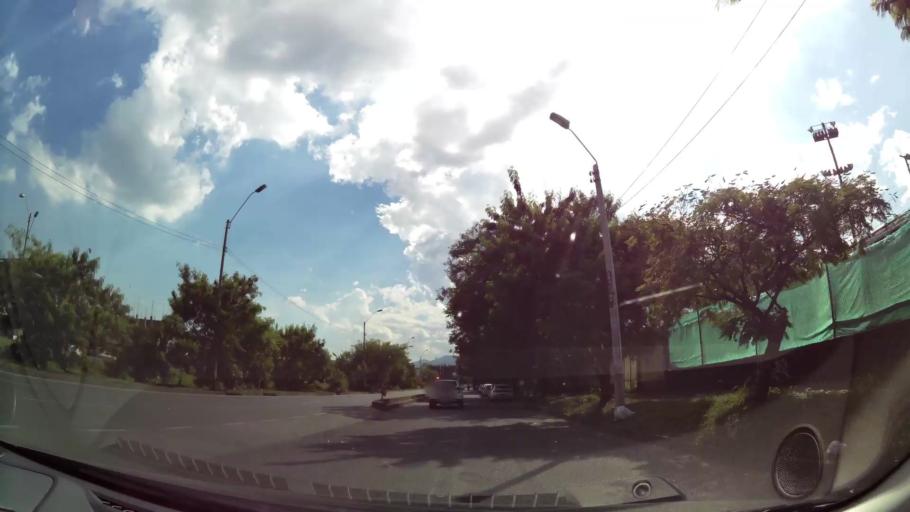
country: CO
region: Valle del Cauca
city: Cali
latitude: 3.4156
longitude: -76.5124
